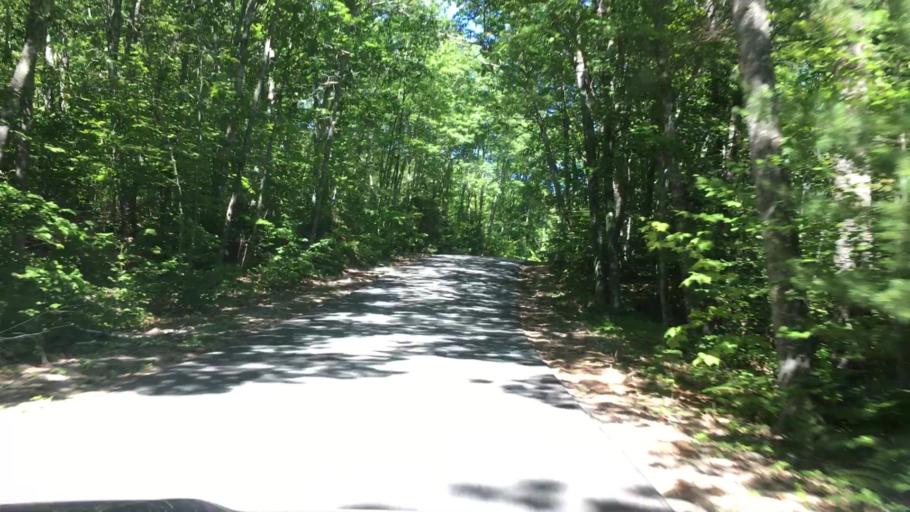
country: US
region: Maine
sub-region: Hancock County
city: Sedgwick
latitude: 44.3331
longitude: -68.6593
